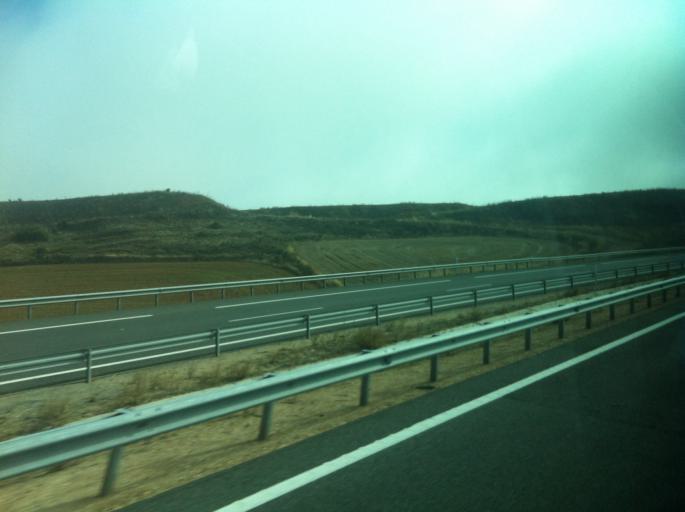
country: ES
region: Castille and Leon
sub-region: Provincia de Burgos
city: Cogollos
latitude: 42.2029
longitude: -3.6968
